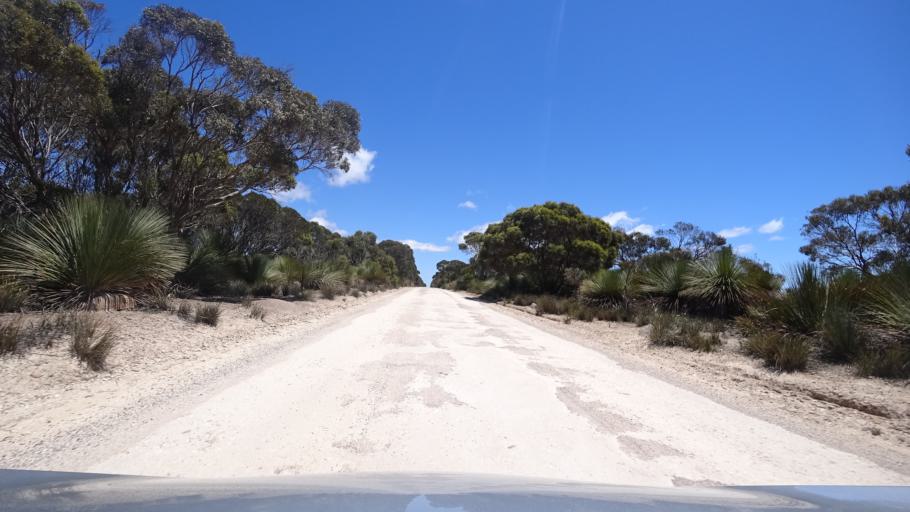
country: AU
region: South Australia
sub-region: Yankalilla
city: Normanville
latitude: -35.8349
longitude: 138.1060
